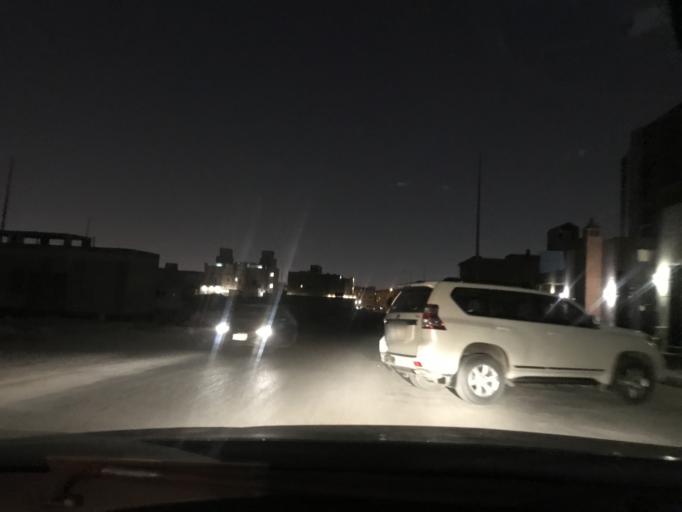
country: SA
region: Ar Riyad
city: Riyadh
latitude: 24.7490
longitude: 46.7558
